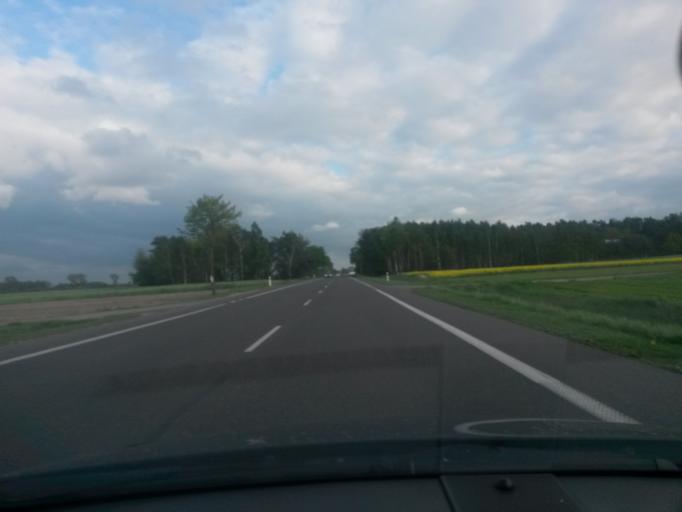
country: PL
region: Masovian Voivodeship
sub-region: Powiat plocki
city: Drobin
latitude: 52.7097
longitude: 20.0291
